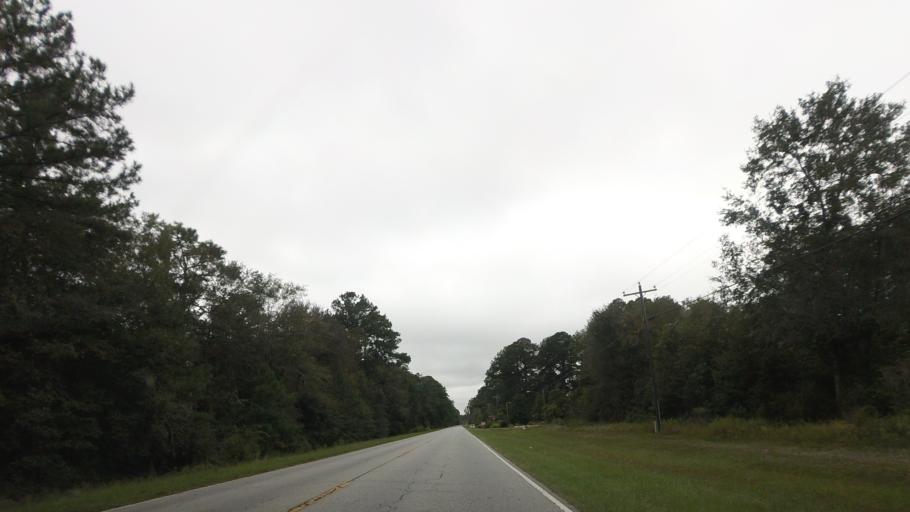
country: US
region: Georgia
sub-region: Lowndes County
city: Valdosta
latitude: 30.8716
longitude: -83.2408
